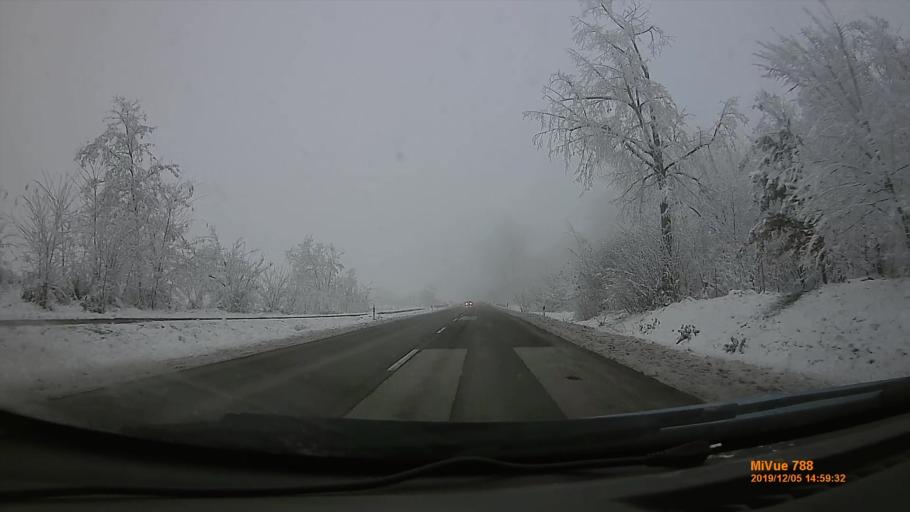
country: HU
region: Szabolcs-Szatmar-Bereg
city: Tiszanagyfalu
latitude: 48.0577
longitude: 21.5555
